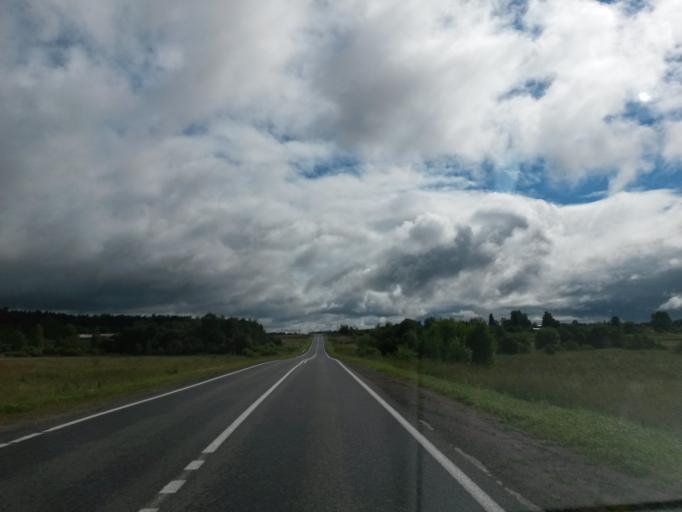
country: RU
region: Jaroslavl
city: Konstantinovskiy
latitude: 57.8217
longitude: 39.6880
